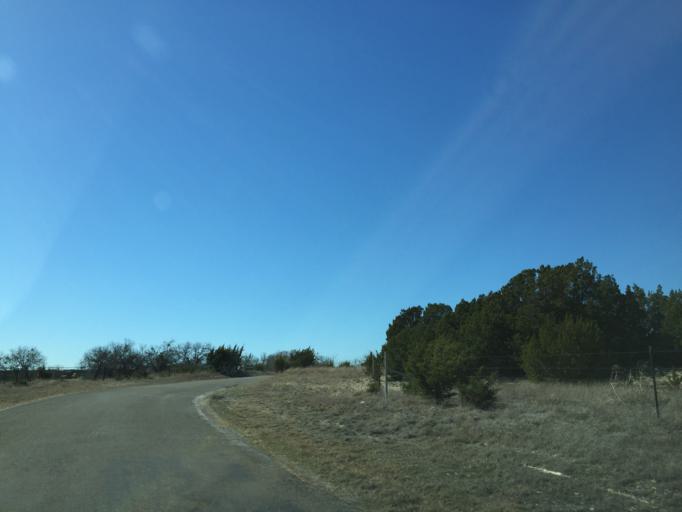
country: US
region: Texas
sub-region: Burnet County
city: Bertram
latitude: 30.9032
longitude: -98.1158
